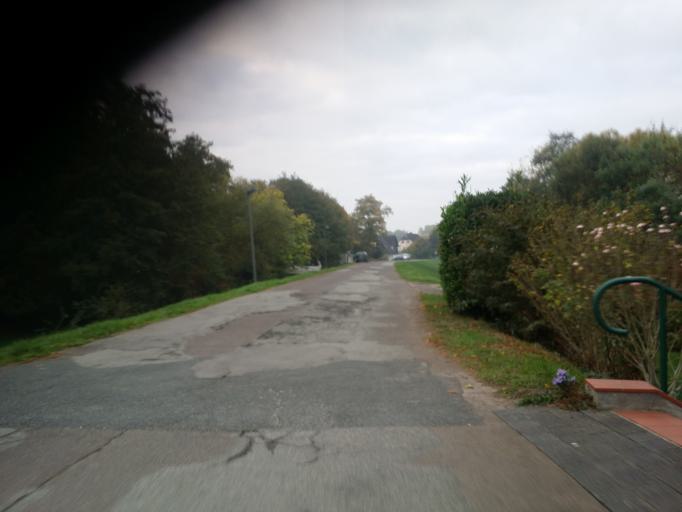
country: DE
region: Lower Saxony
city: Ritterhude
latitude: 53.1580
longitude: 8.7094
